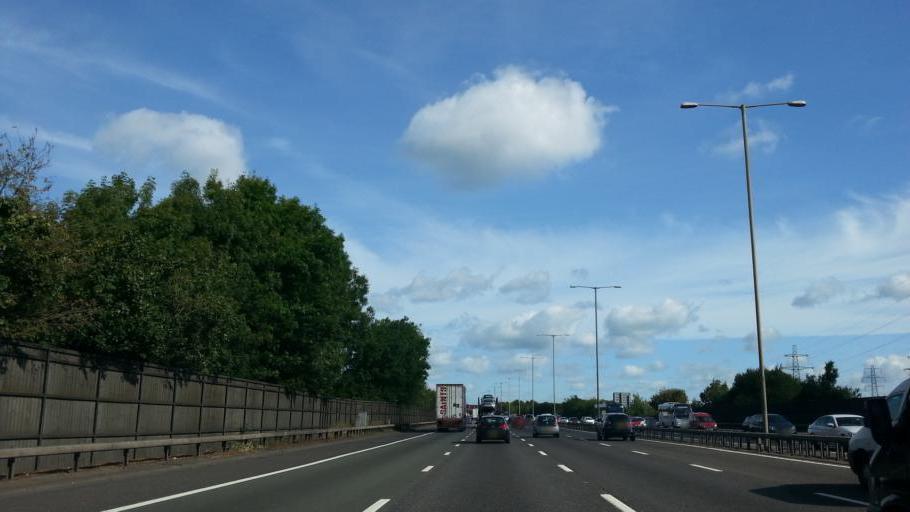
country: GB
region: England
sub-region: Buckinghamshire
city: Iver
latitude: 51.5232
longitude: -0.4986
